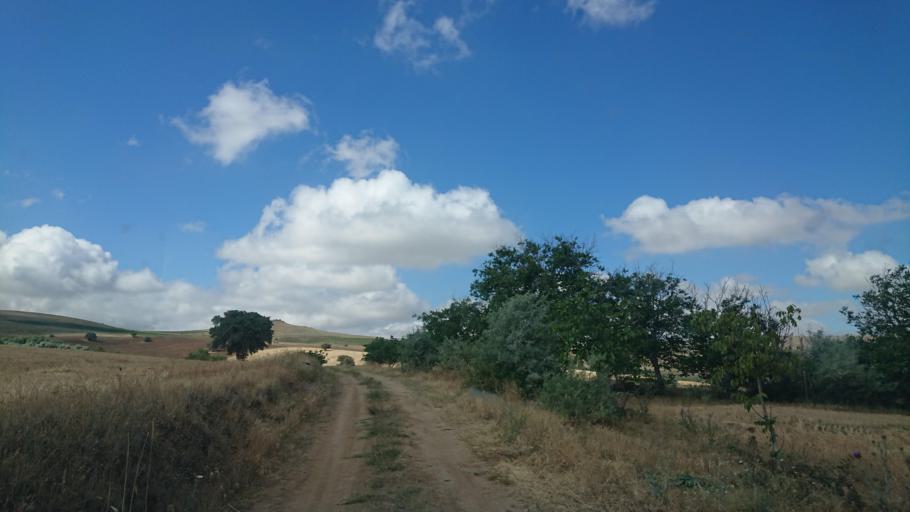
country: TR
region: Aksaray
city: Agacoren
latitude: 38.8465
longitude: 33.9369
